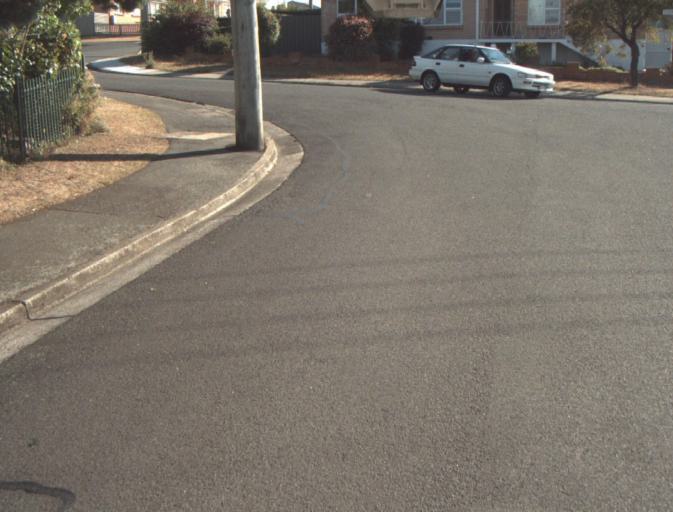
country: AU
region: Tasmania
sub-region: Launceston
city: Invermay
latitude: -41.3936
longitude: 147.1303
